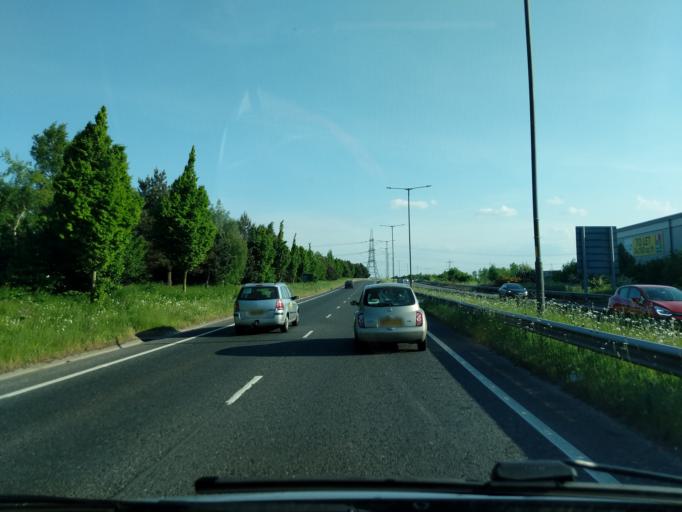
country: GB
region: England
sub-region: St. Helens
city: St Helens
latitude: 53.4266
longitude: -2.7402
